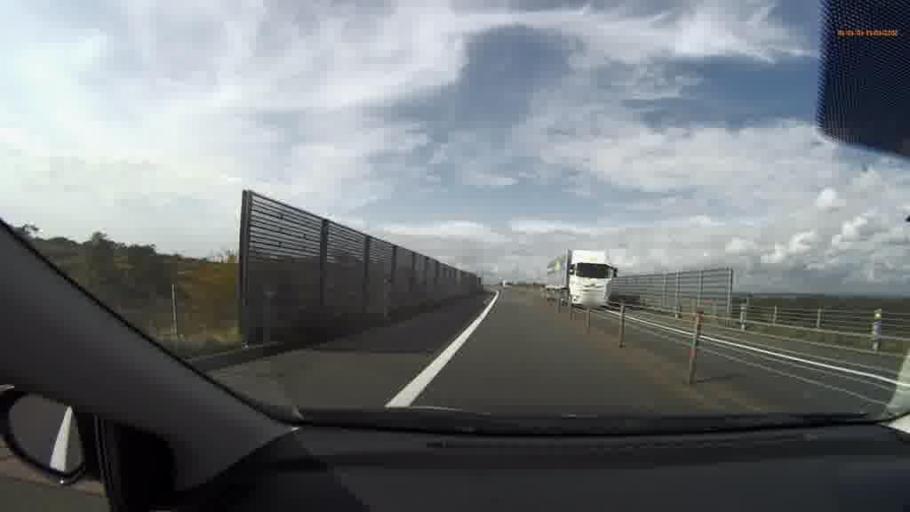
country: JP
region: Hokkaido
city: Kushiro
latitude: 43.0347
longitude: 144.3736
